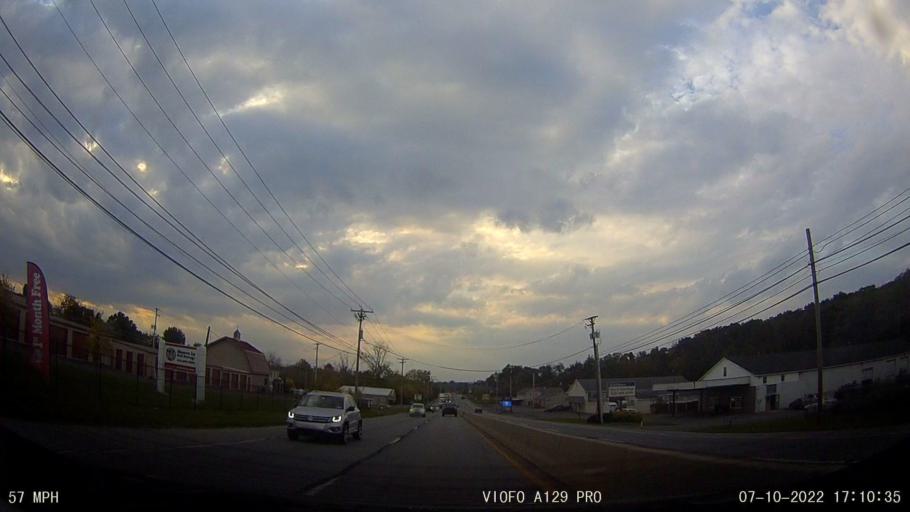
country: US
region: Pennsylvania
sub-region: Berks County
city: Amity Gardens
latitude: 40.2683
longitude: -75.7631
